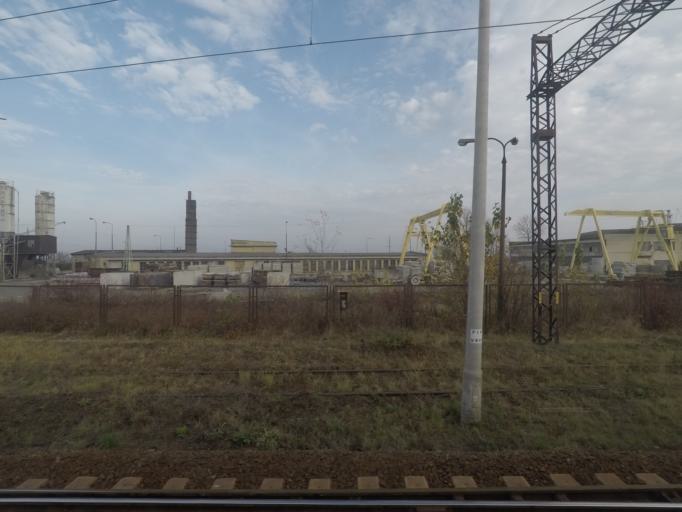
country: PL
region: Subcarpathian Voivodeship
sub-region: Powiat jaroslawski
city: Radymno
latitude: 49.9334
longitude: 22.8372
